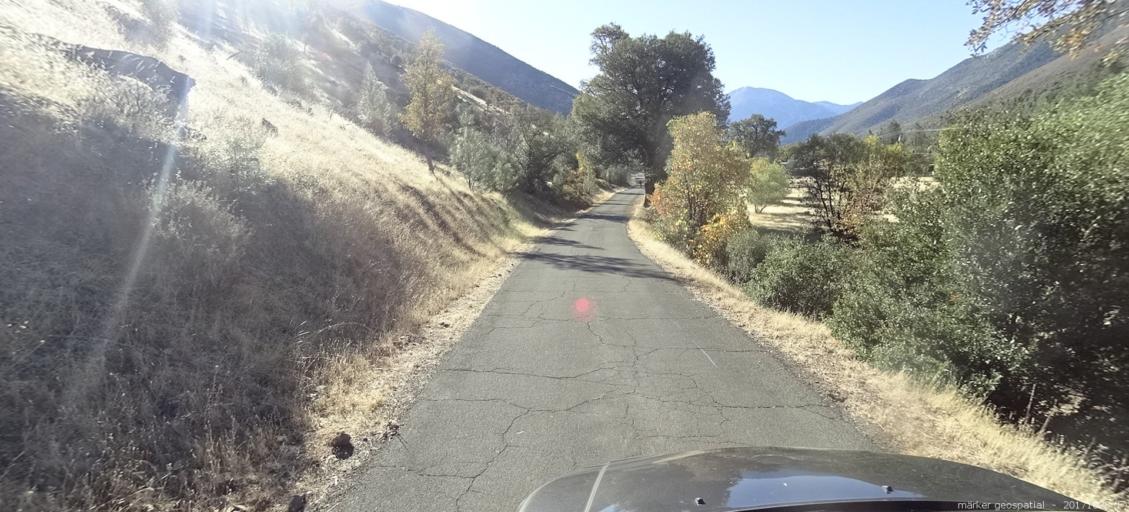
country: US
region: California
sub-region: Trinity County
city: Lewiston
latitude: 40.7109
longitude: -122.6349
